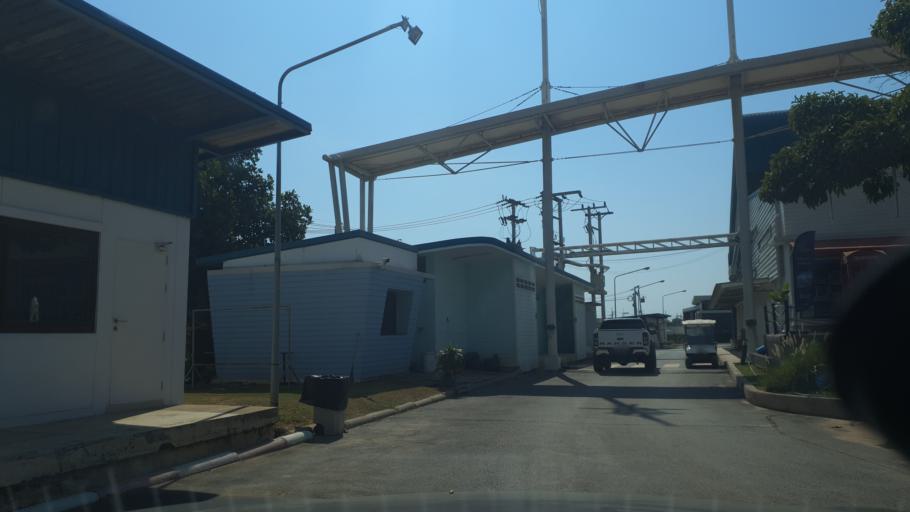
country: TH
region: Samut Sakhon
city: Samut Sakhon
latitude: 13.5296
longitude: 100.2016
